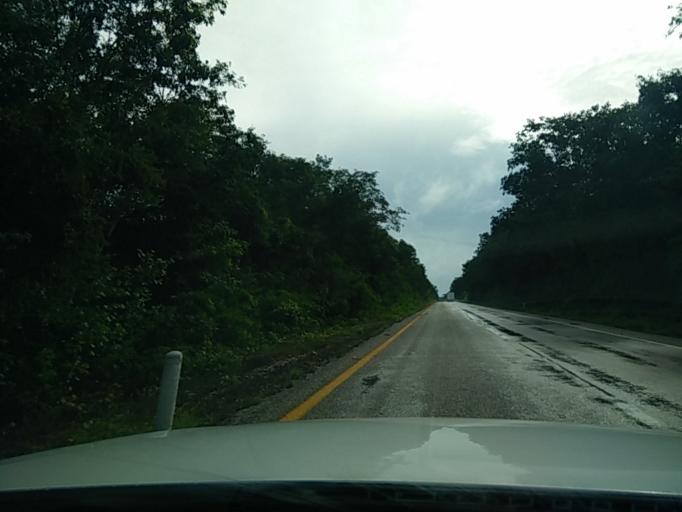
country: MX
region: Yucatan
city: Tunkas
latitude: 20.7531
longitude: -88.7354
